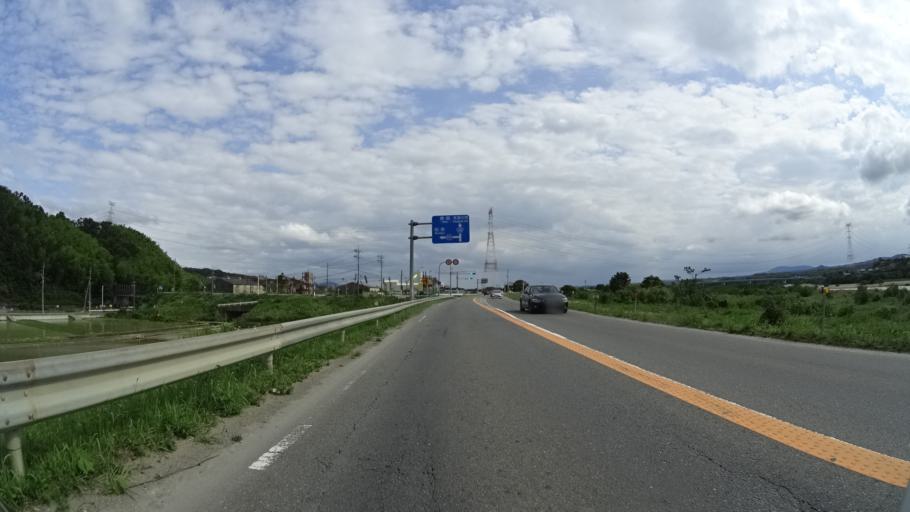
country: JP
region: Kyoto
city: Tanabe
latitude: 34.8084
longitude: 135.8052
